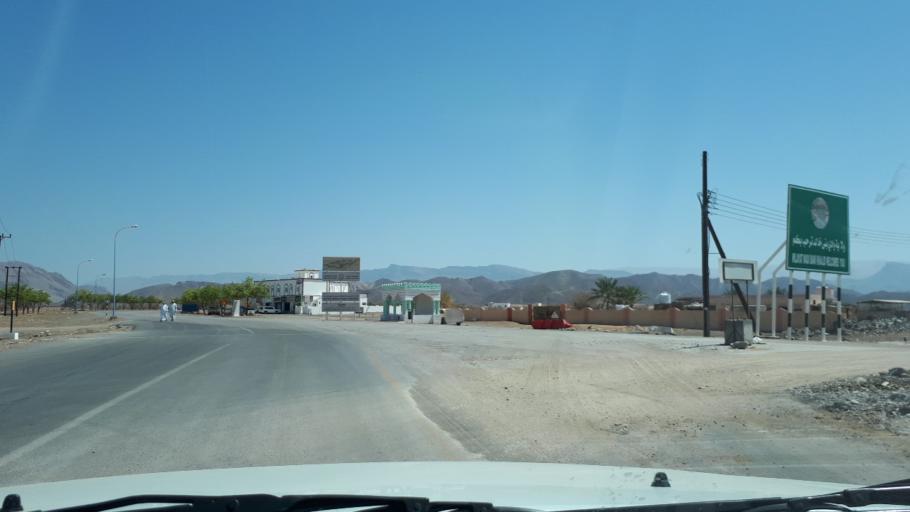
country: OM
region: Ash Sharqiyah
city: Badiyah
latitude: 22.4946
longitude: 58.9379
